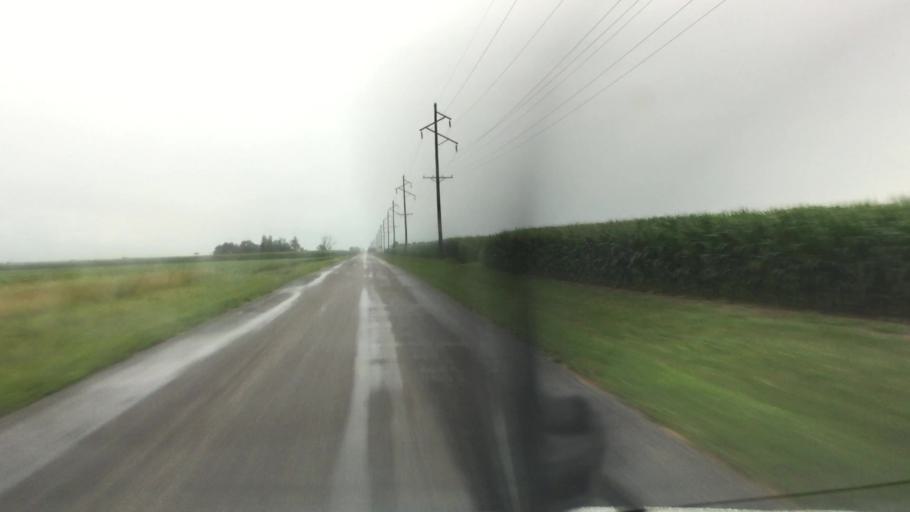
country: US
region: Illinois
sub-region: Hancock County
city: Nauvoo
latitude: 40.5144
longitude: -91.2693
